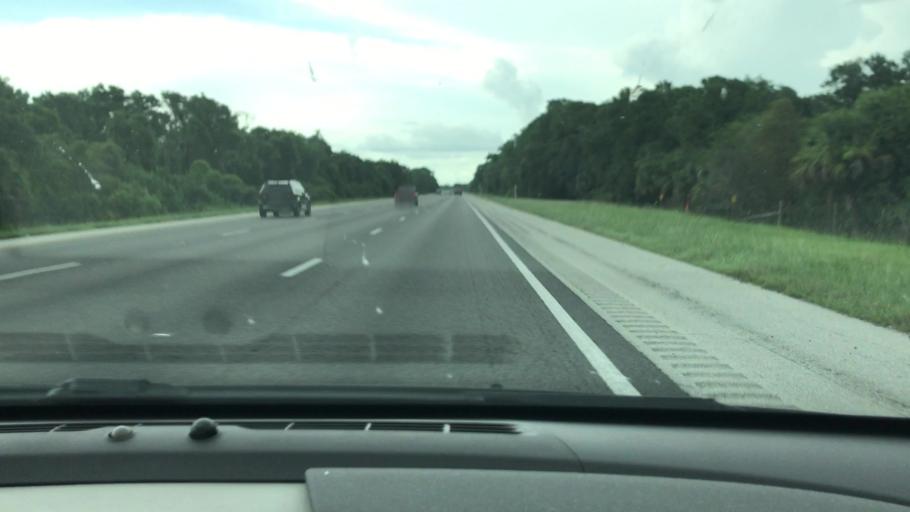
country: US
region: Florida
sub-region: Sarasota County
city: Vamo
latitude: 27.2385
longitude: -82.4515
